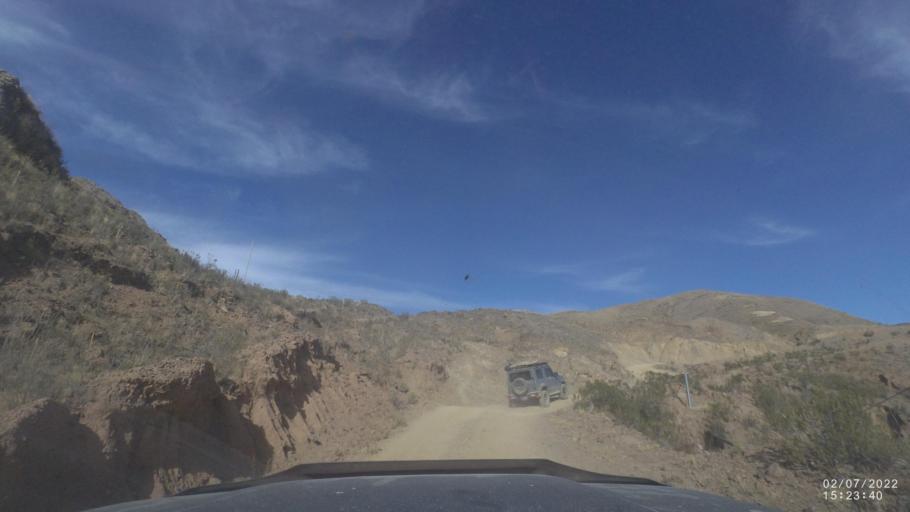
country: BO
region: Cochabamba
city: Irpa Irpa
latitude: -17.8742
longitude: -66.4188
